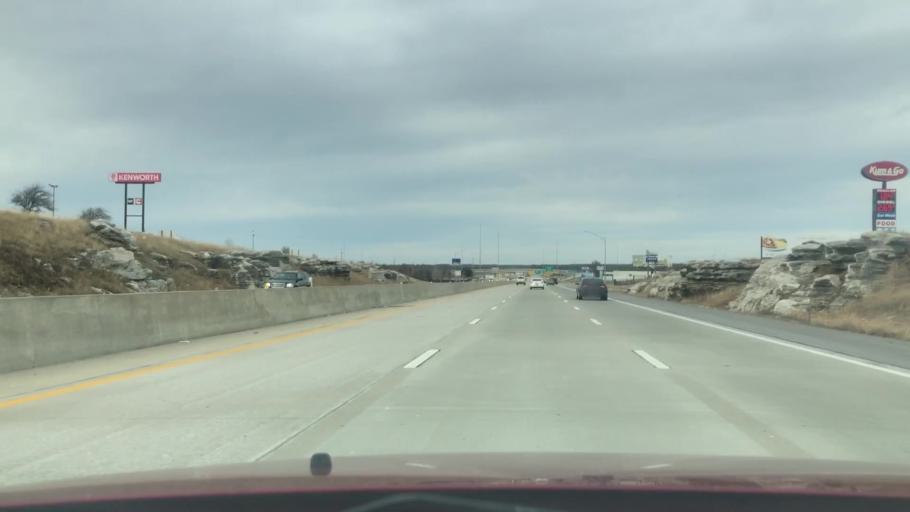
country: US
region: Missouri
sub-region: Greene County
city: Springfield
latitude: 37.2393
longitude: -93.2246
